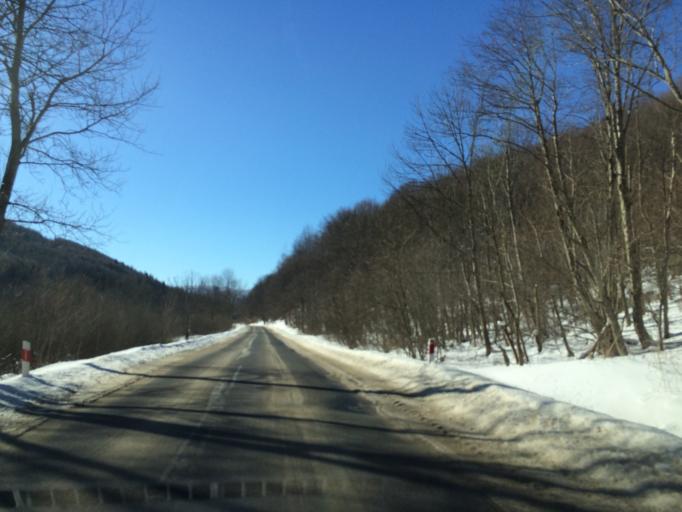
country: PL
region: Subcarpathian Voivodeship
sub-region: Powiat bieszczadzki
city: Lutowiska
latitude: 49.1245
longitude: 22.6686
